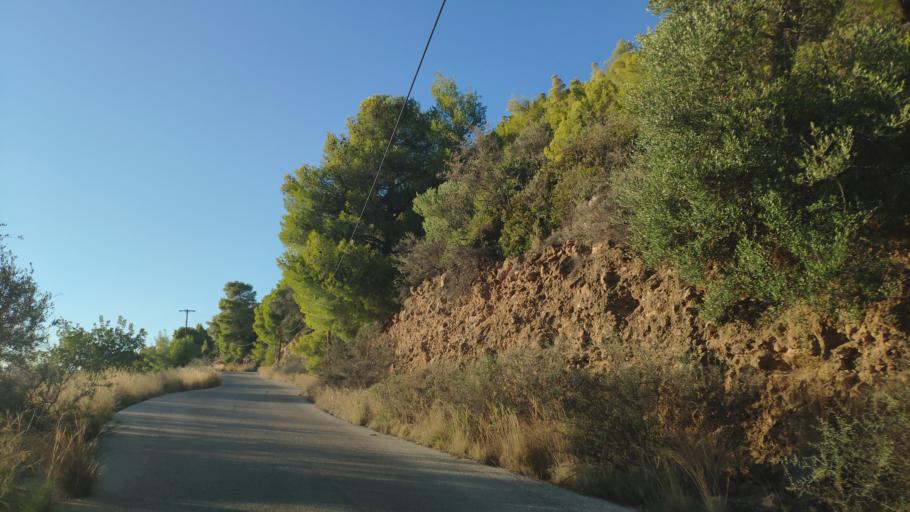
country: GR
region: Attica
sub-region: Nomos Piraios
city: Megalochori
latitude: 37.6017
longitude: 23.3342
